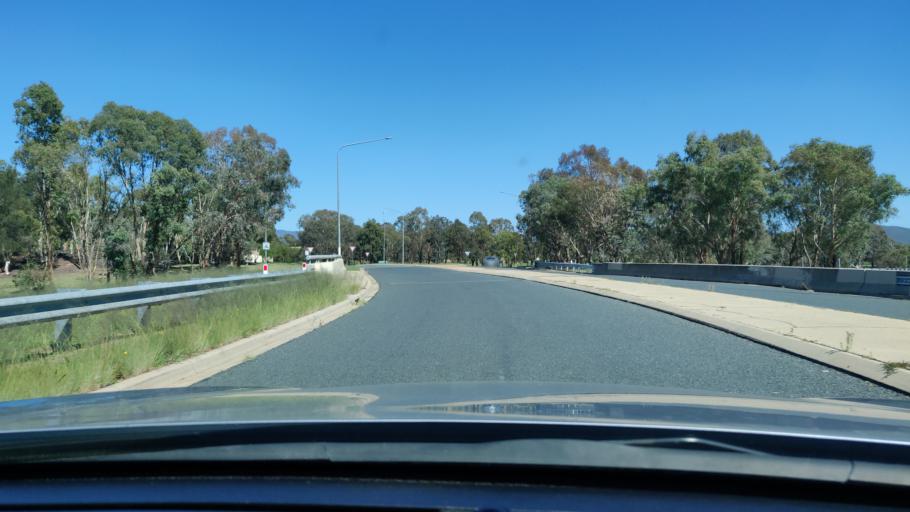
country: AU
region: Australian Capital Territory
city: Macarthur
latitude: -35.4287
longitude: 149.0869
